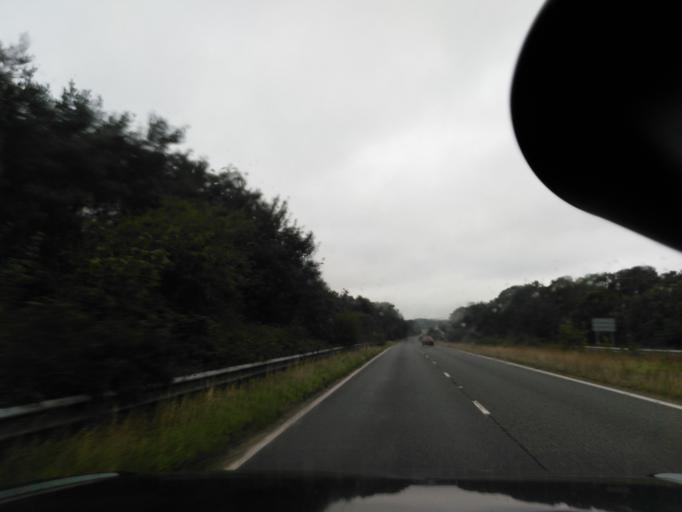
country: GB
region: England
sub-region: Dorset
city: Broadstone
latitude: 50.7398
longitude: -2.0151
